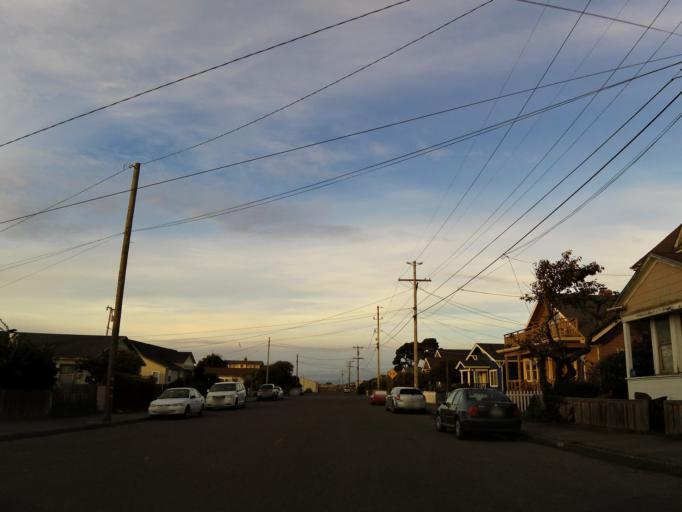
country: US
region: California
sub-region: Mendocino County
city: Fort Bragg
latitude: 39.4486
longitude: -123.8087
